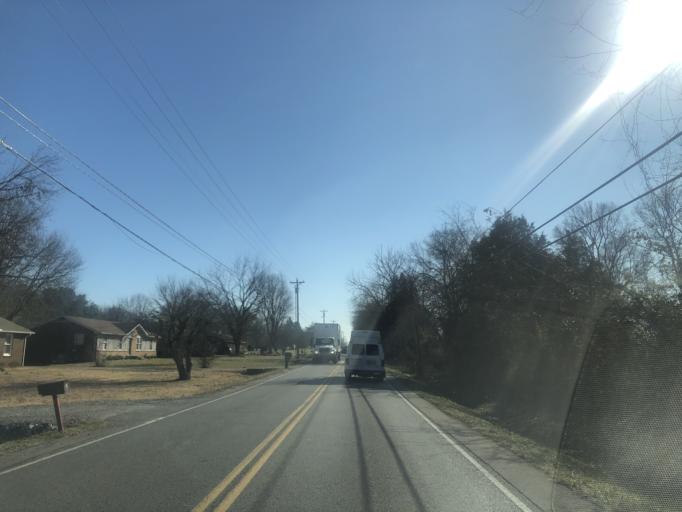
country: US
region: Tennessee
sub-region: Rutherford County
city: Smyrna
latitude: 35.9234
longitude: -86.4808
